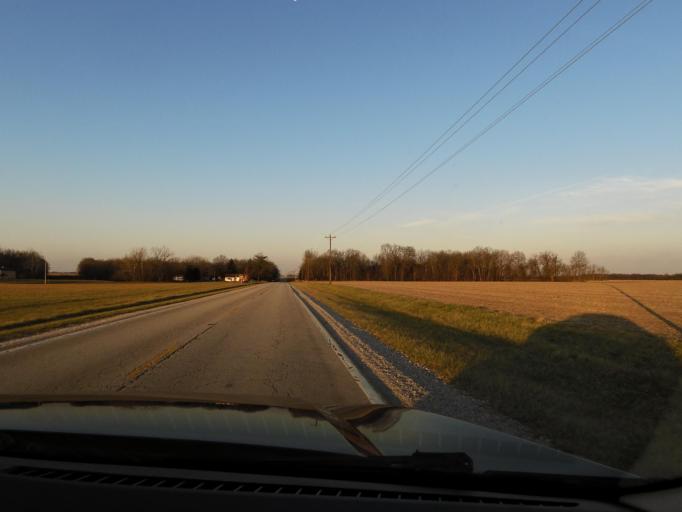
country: US
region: Illinois
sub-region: Marion County
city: Salem
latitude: 38.7653
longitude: -88.9778
